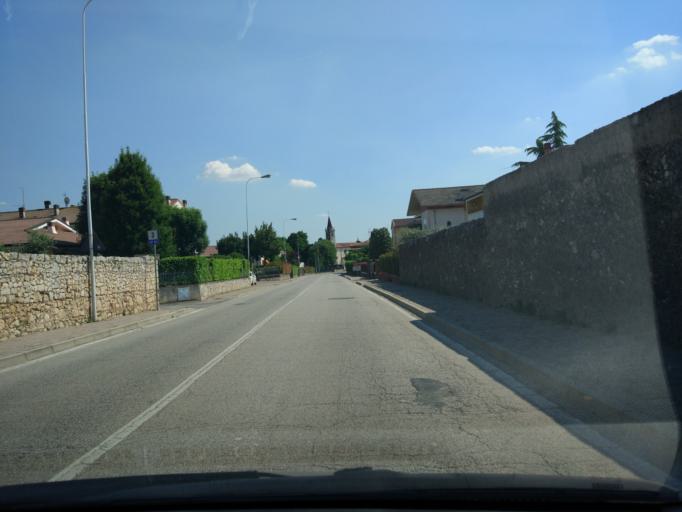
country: IT
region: Veneto
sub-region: Provincia di Verona
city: Colognola ai Colli
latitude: 45.4432
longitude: 11.1787
